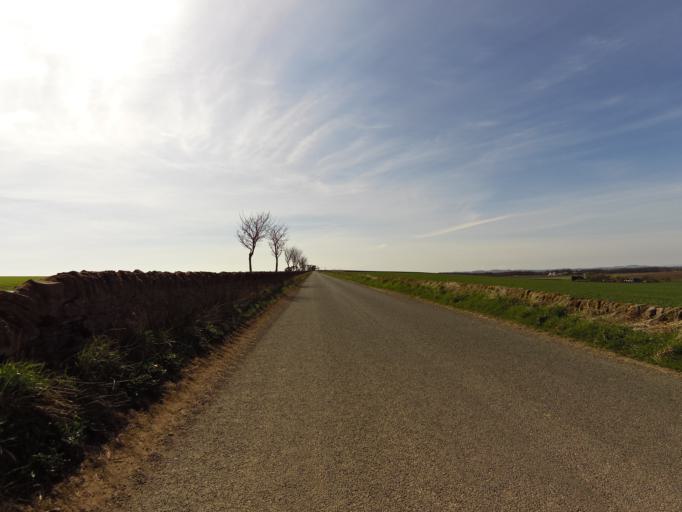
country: GB
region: Scotland
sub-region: Angus
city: Arbroath
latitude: 56.6050
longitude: -2.5274
